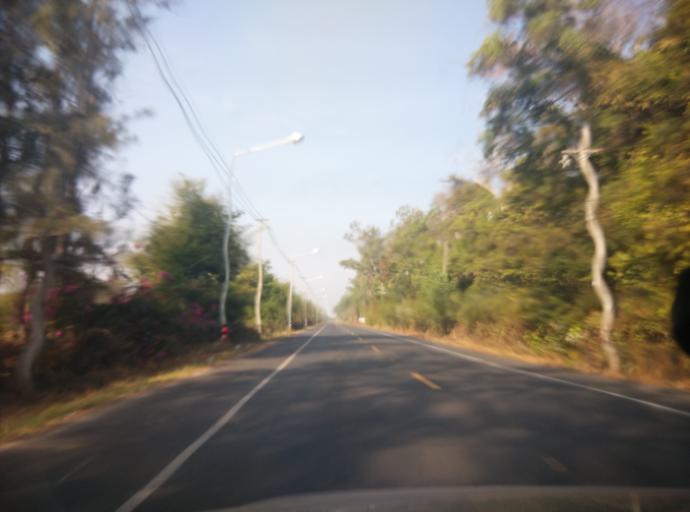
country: TH
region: Sisaket
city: Si Sa Ket
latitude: 15.1117
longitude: 104.2824
